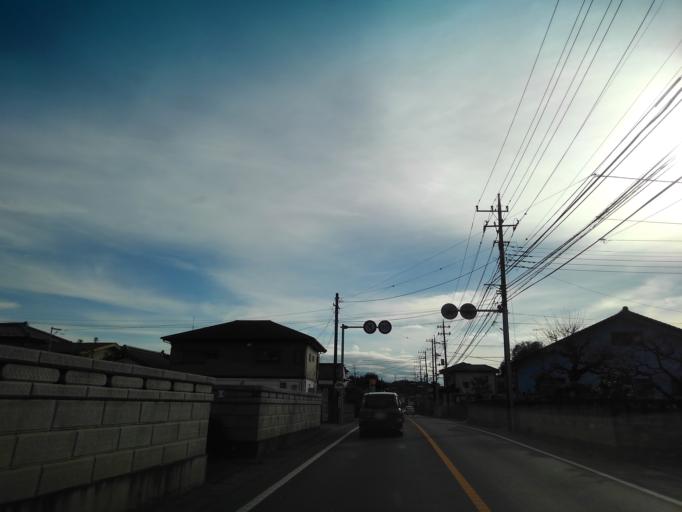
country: JP
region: Saitama
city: Hanno
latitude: 35.8906
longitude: 139.3388
